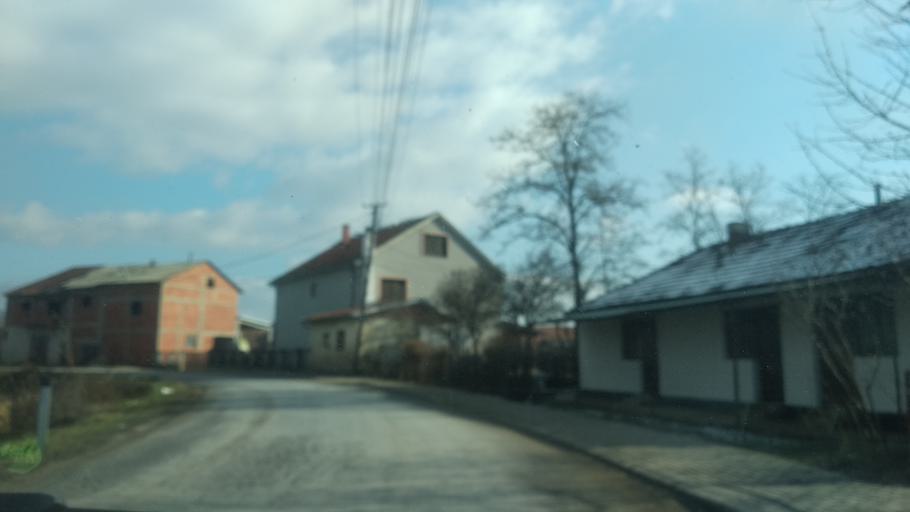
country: XK
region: Pristina
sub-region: Lipjan
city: Lipljan
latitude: 42.5934
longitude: 21.1421
